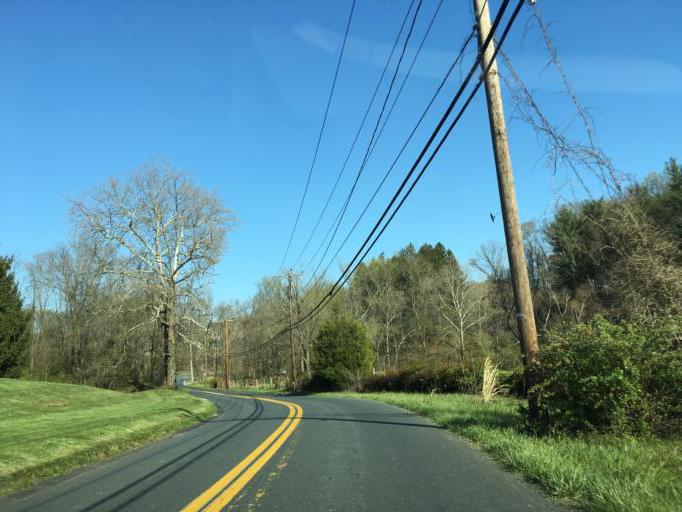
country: US
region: Maryland
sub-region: Baltimore County
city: Perry Hall
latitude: 39.4701
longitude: -76.4938
